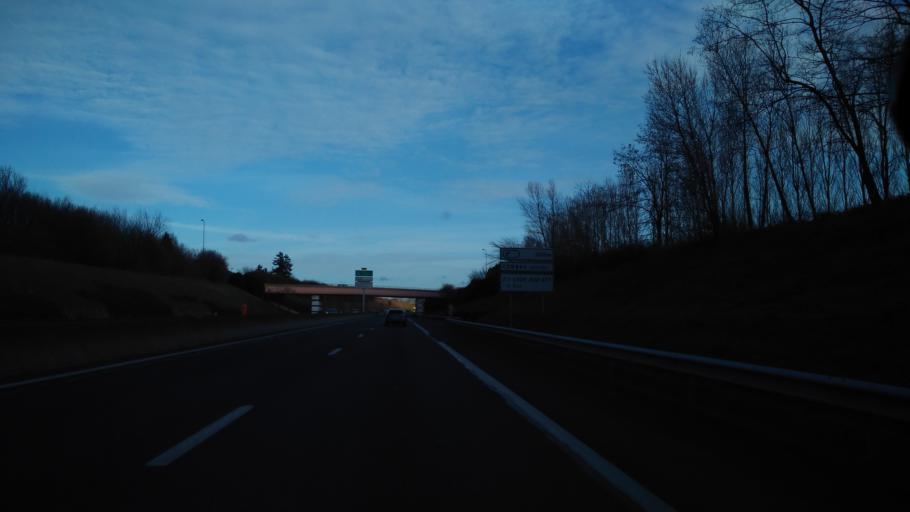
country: FR
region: Rhone-Alpes
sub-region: Departement du Rhone
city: Corbas
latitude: 45.6806
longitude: 4.8924
